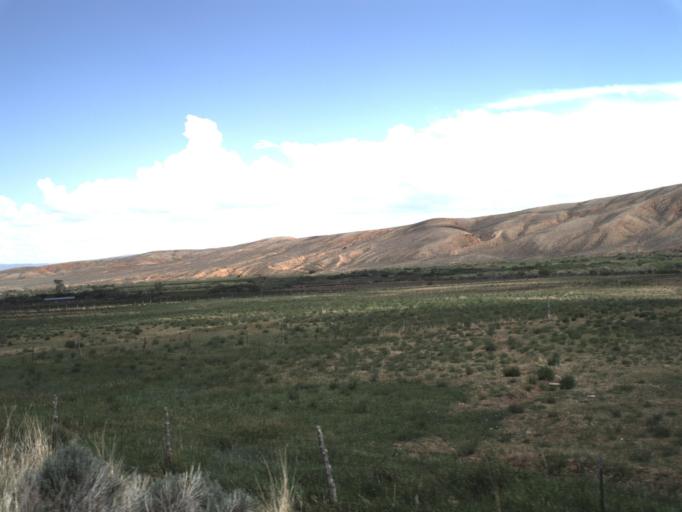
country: US
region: Utah
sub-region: Rich County
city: Randolph
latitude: 41.5011
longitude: -111.2489
